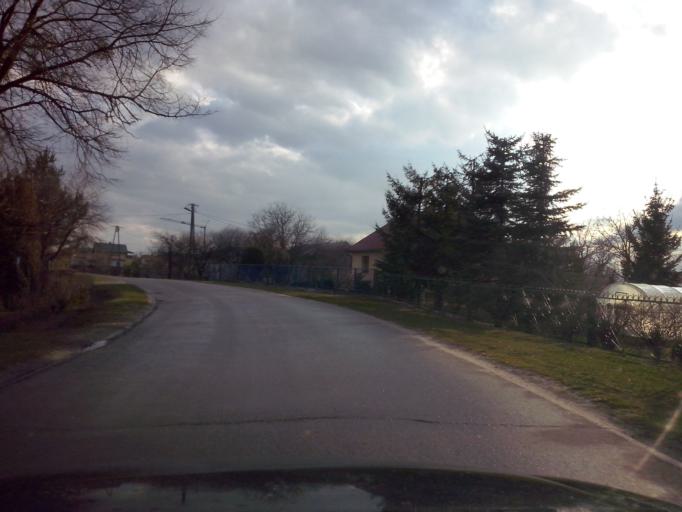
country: PL
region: Lublin Voivodeship
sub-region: Chelm
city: Chelm
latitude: 51.1540
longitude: 23.5416
